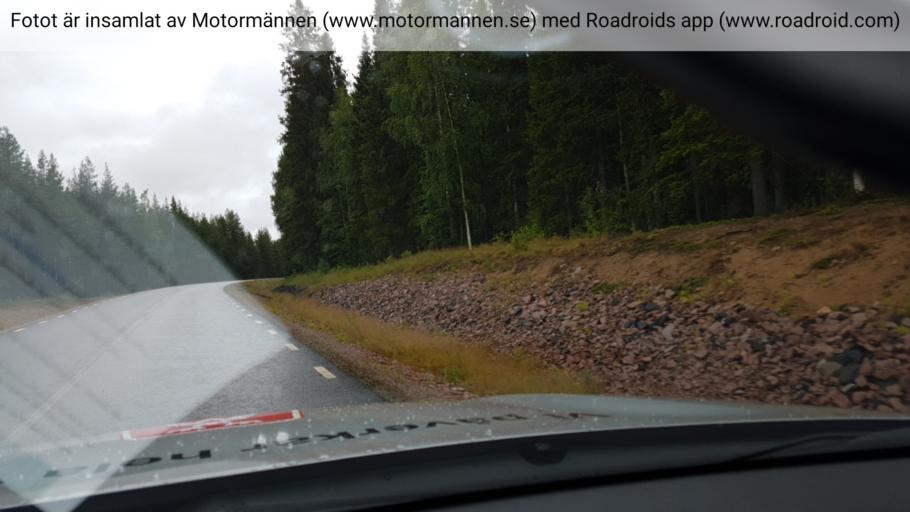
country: SE
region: Norrbotten
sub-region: Gallivare Kommun
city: Gaellivare
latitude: 66.6461
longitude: 20.3912
